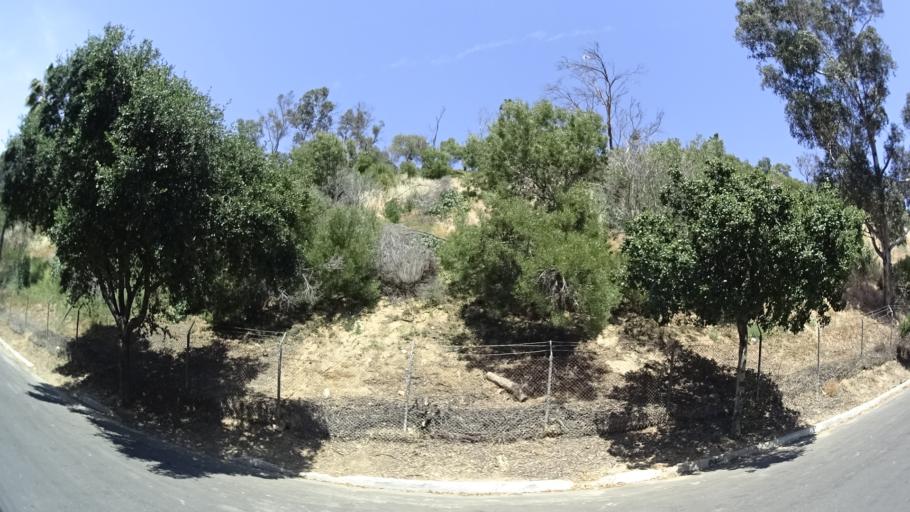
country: US
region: California
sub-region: Los Angeles County
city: Los Angeles
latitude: 34.0706
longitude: -118.2433
